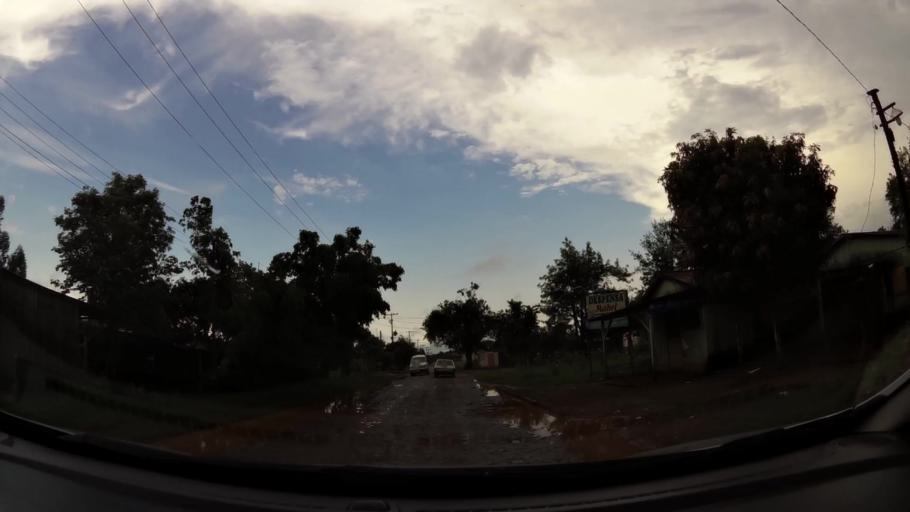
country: PY
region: Alto Parana
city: Presidente Franco
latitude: -25.5349
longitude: -54.6609
